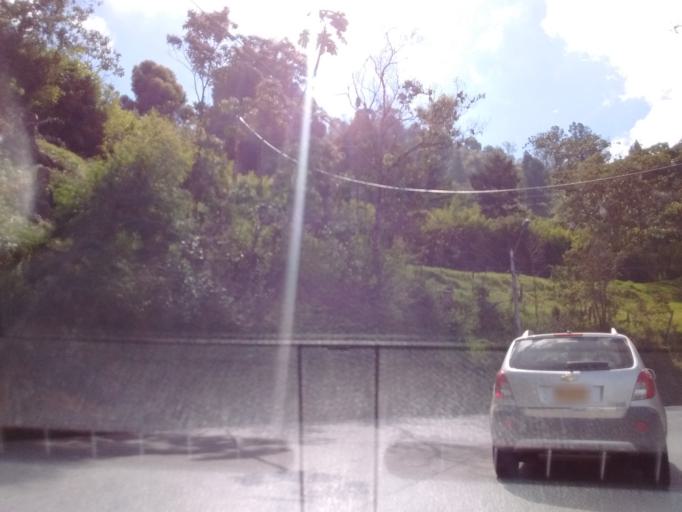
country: CO
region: Antioquia
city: Medellin
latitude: 6.2444
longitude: -75.5140
